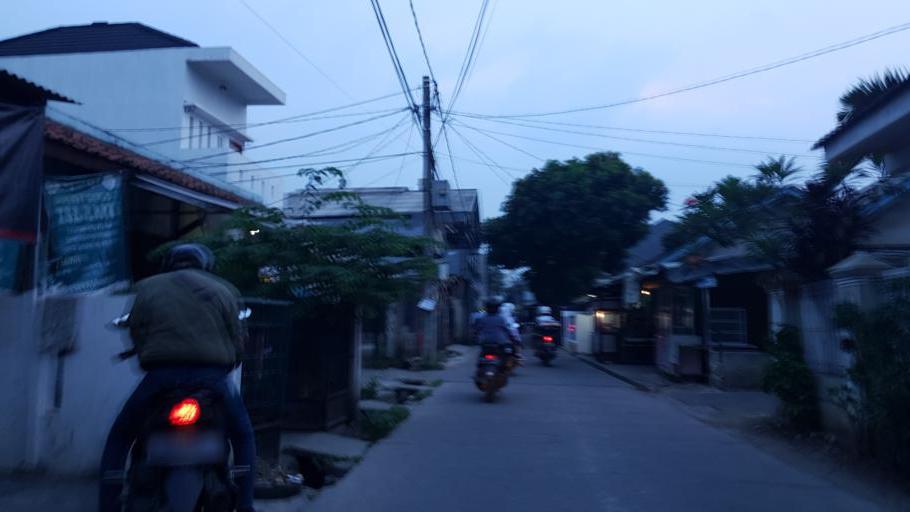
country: ID
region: West Java
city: Pamulang
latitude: -6.3295
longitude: 106.7935
